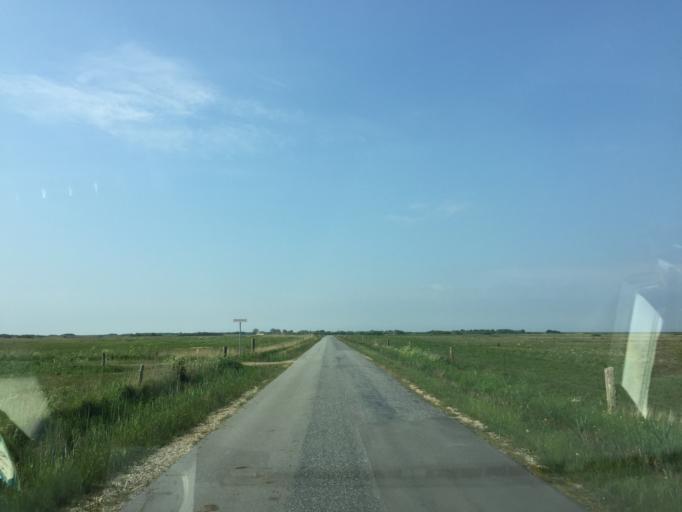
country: DK
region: South Denmark
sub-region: Esbjerg Kommune
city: Tjaereborg
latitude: 55.2884
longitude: 8.5653
